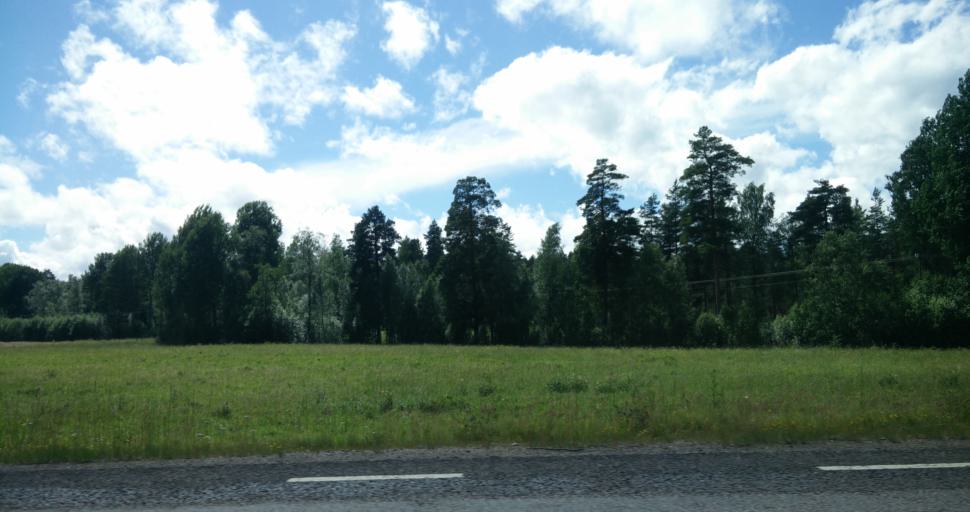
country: SE
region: Vaermland
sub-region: Hagfors Kommun
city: Hagfors
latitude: 60.0155
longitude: 13.6285
